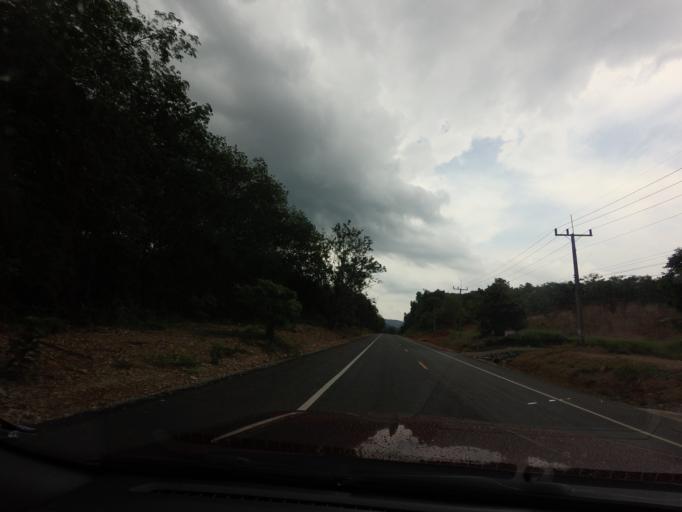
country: TH
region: Yala
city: Ban Nang Sata
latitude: 6.2311
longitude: 101.2174
